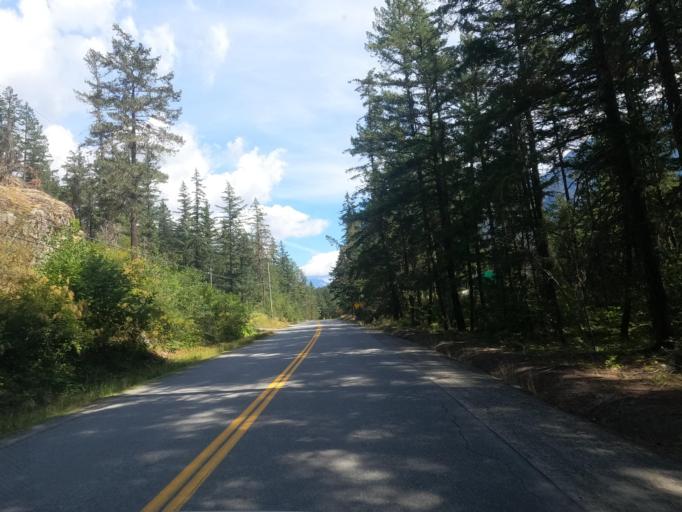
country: CA
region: British Columbia
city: Pemberton
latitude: 50.3371
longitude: -122.7292
